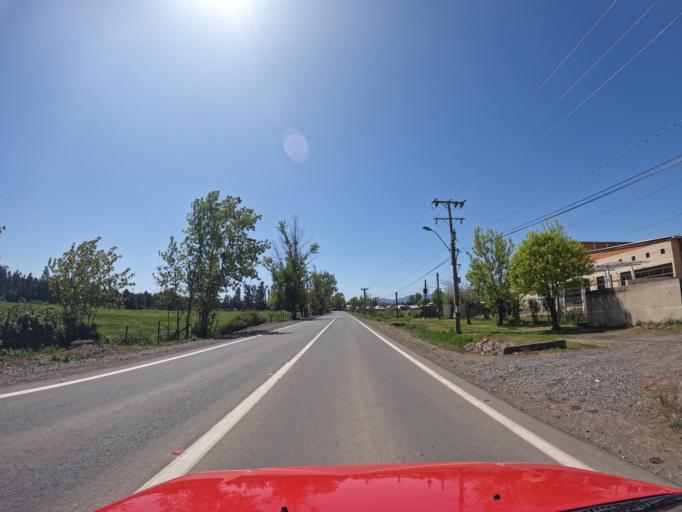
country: CL
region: Maule
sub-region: Provincia de Linares
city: Colbun
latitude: -35.7582
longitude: -71.4191
